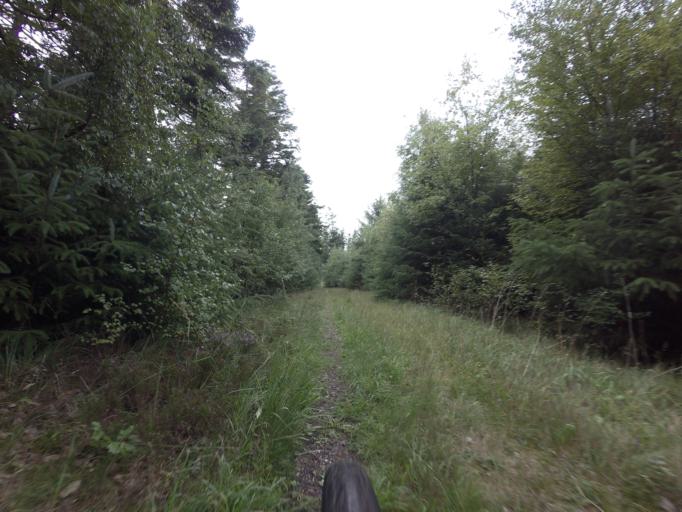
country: DK
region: North Denmark
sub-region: Hjorring Kommune
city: Hirtshals
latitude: 57.5779
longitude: 10.0425
